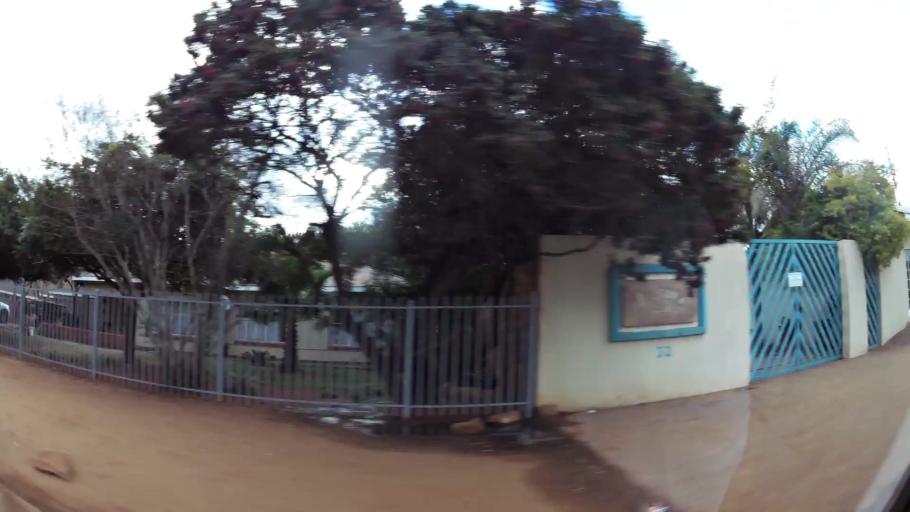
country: ZA
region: Limpopo
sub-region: Waterberg District Municipality
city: Modimolle
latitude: -24.5202
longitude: 28.7114
